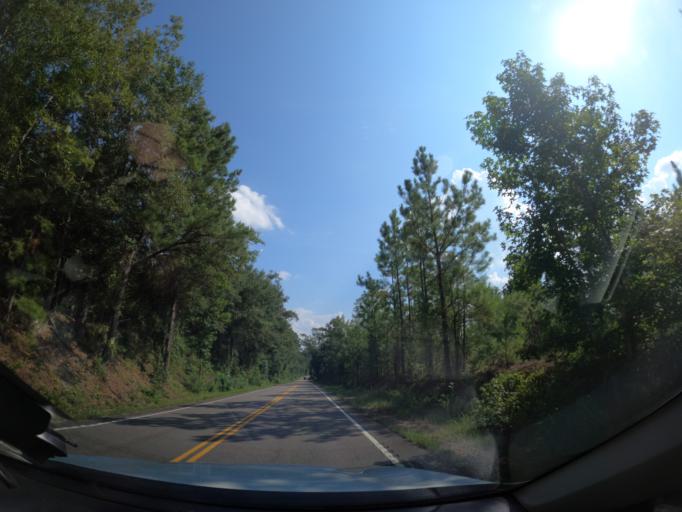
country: US
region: South Carolina
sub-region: Barnwell County
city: Williston
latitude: 33.5633
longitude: -81.4817
